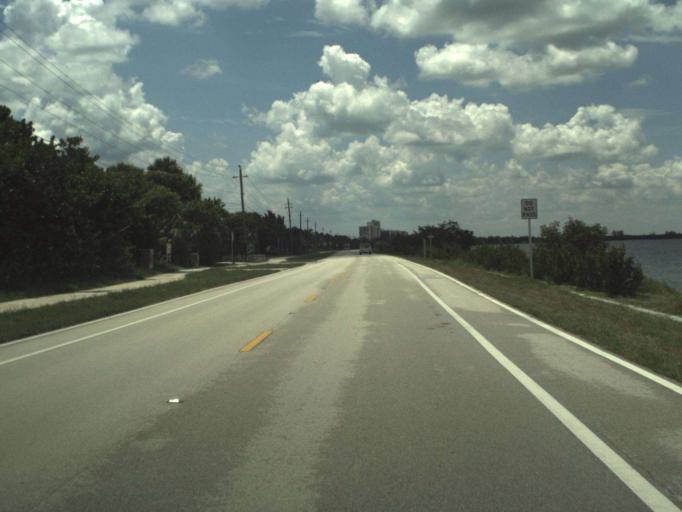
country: US
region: Florida
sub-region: Saint Lucie County
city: Hutchinson Island South
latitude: 27.3220
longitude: -80.2283
